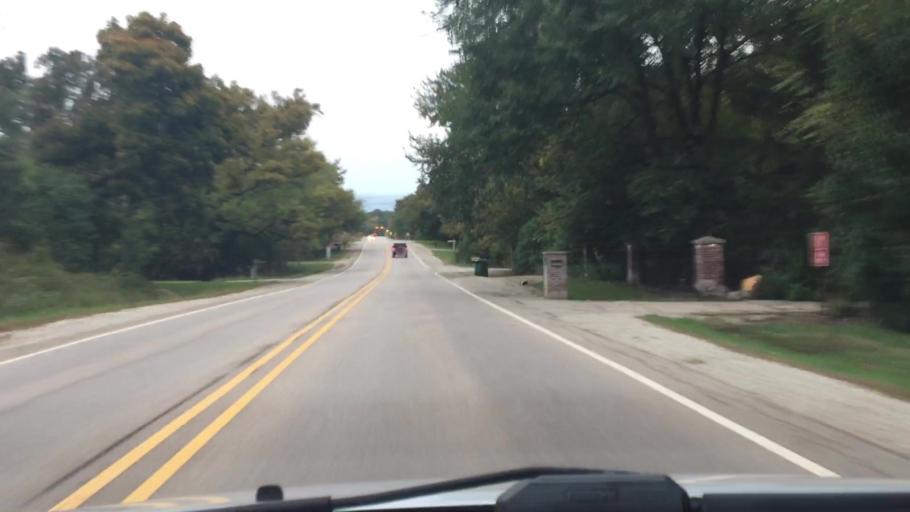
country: US
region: Illinois
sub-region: Kane County
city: Farmington
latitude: 41.9633
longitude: -88.3204
